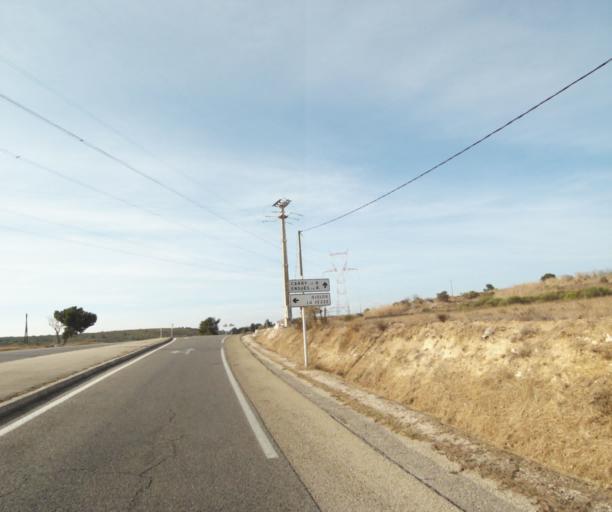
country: FR
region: Provence-Alpes-Cote d'Azur
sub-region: Departement des Bouches-du-Rhone
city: Le Rove
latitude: 43.3605
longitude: 5.2317
